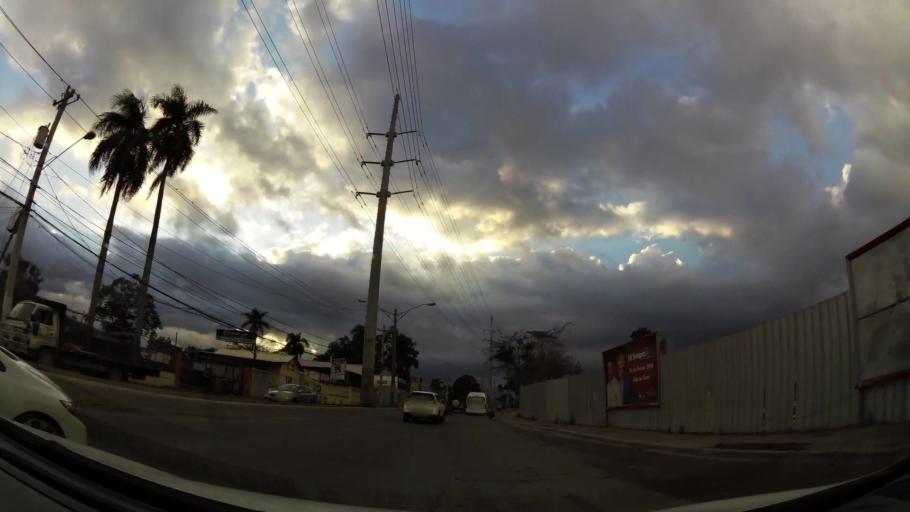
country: DO
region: Nacional
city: Santo Domingo
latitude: 18.5068
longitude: -69.9850
